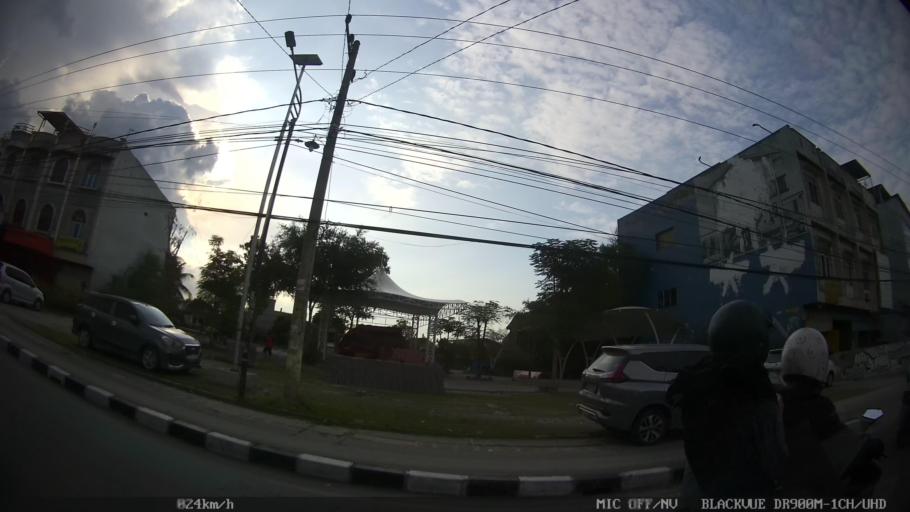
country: ID
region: North Sumatra
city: Sunggal
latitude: 3.5618
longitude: 98.6377
